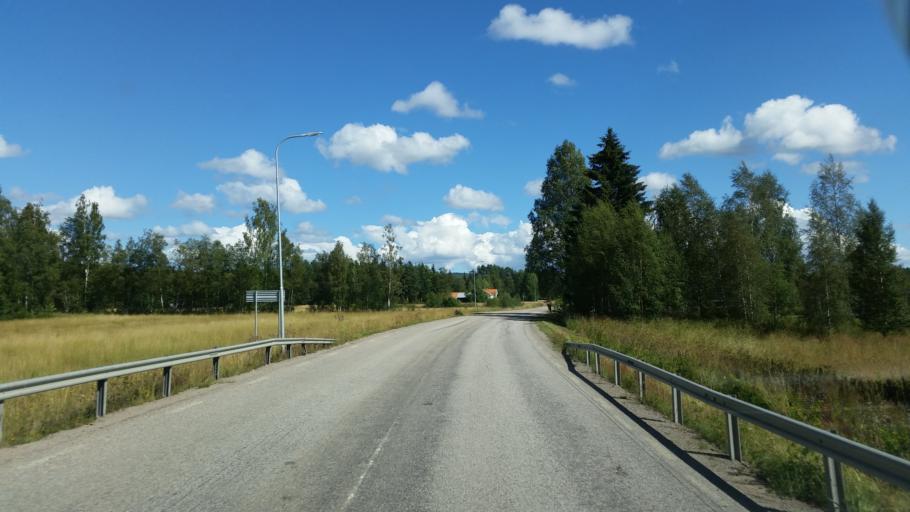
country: SE
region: Gaevleborg
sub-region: Ljusdals Kommun
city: Ljusdal
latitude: 61.8385
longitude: 16.1198
